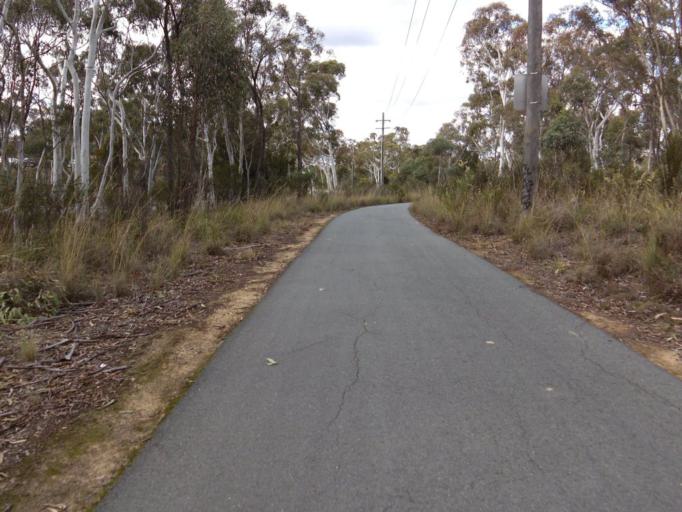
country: AU
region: Australian Capital Territory
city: Macquarie
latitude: -35.2514
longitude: 149.0954
